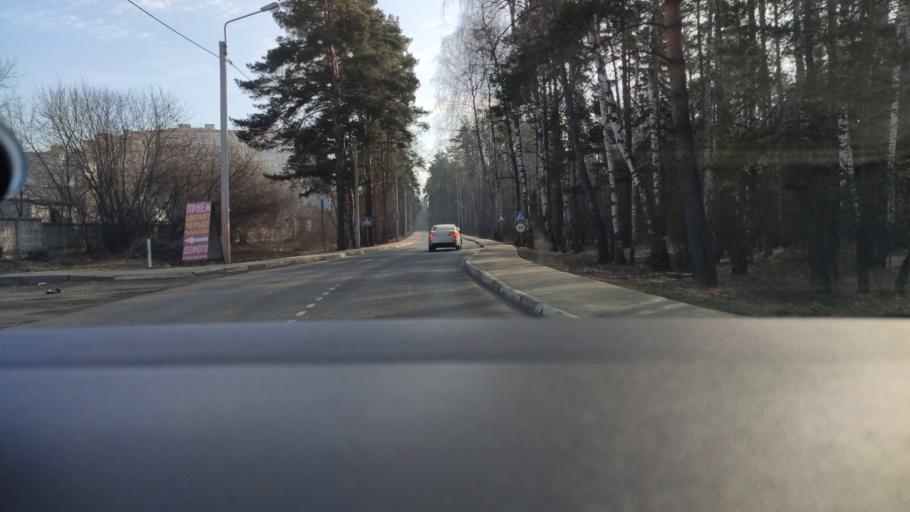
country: RU
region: Moskovskaya
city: Zarya
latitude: 55.8070
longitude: 38.0929
